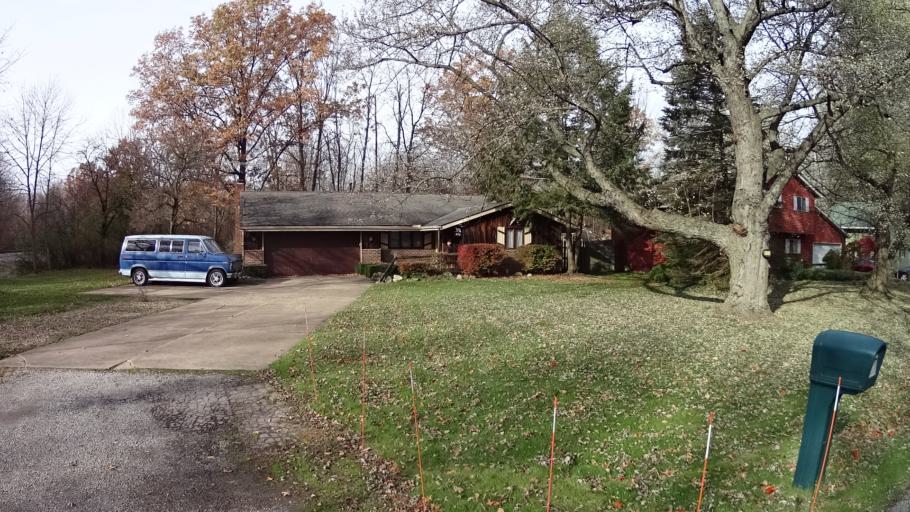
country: US
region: Ohio
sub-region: Lorain County
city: Sheffield Lake
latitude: 41.4789
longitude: -82.1221
